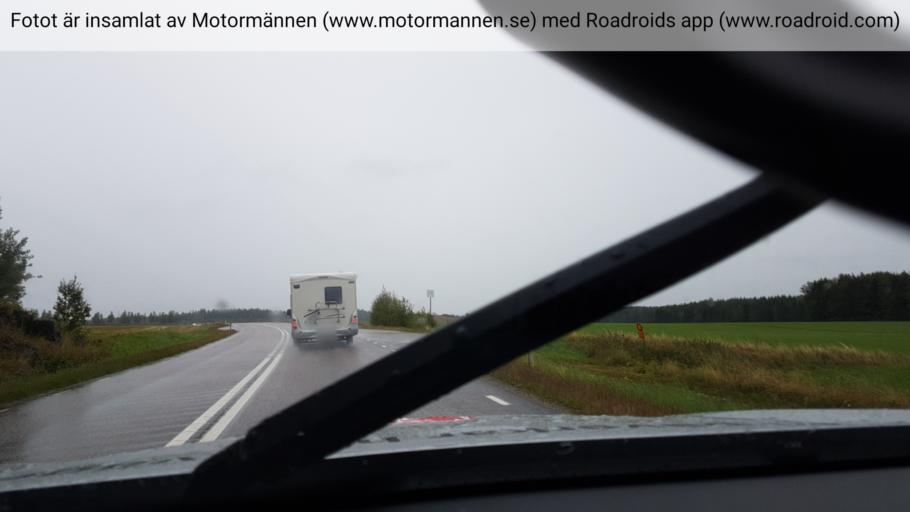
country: SE
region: Vaestra Goetaland
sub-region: Vargarda Kommun
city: Jonstorp
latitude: 58.0934
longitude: 12.6588
